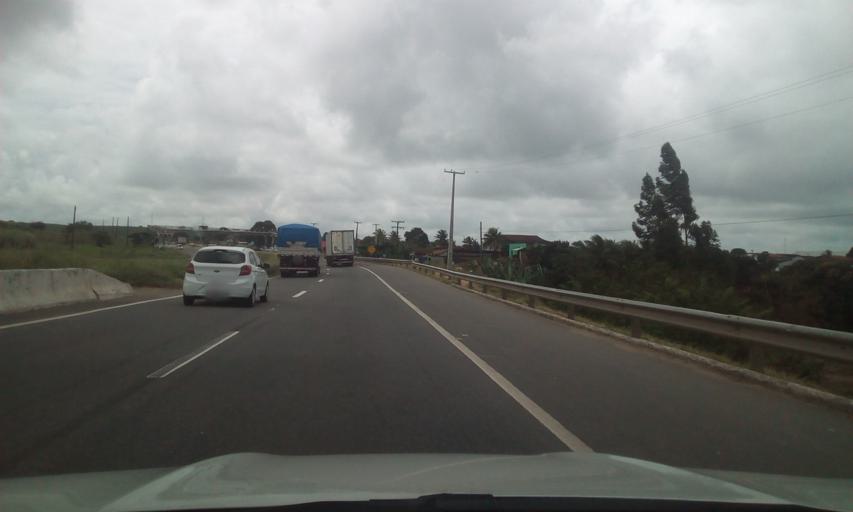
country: BR
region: Pernambuco
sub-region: Itapissuma
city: Itapissuma
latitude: -7.7513
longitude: -34.9362
